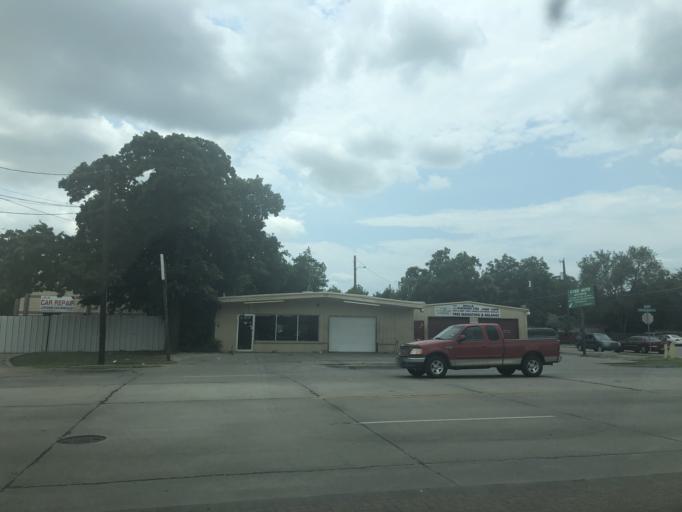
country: US
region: Texas
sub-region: Dallas County
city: Irving
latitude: 32.8012
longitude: -96.9321
